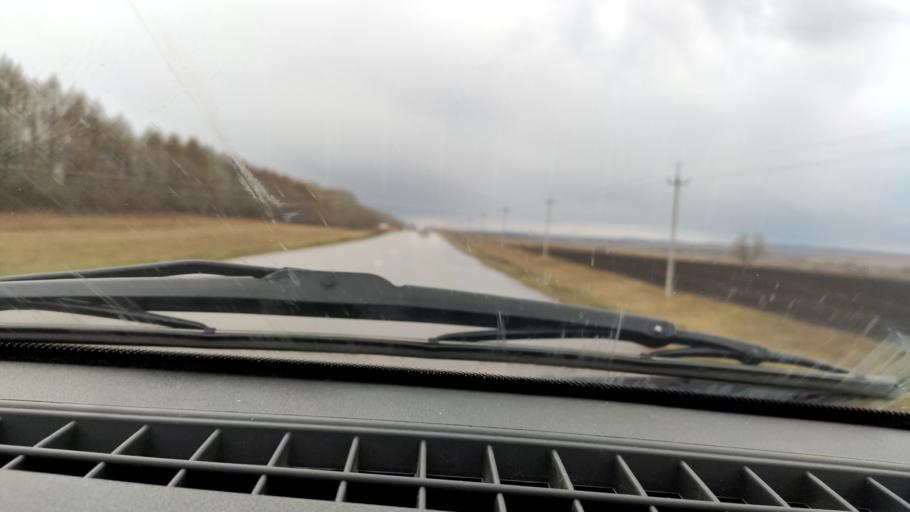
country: RU
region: Bashkortostan
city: Chekmagush
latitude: 55.1119
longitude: 54.9077
